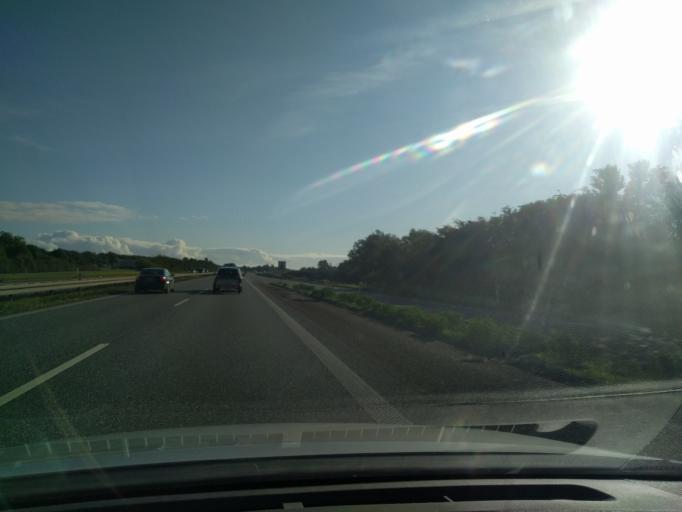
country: DK
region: Zealand
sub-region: Soro Kommune
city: Frederiksberg
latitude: 55.4529
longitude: 11.6027
